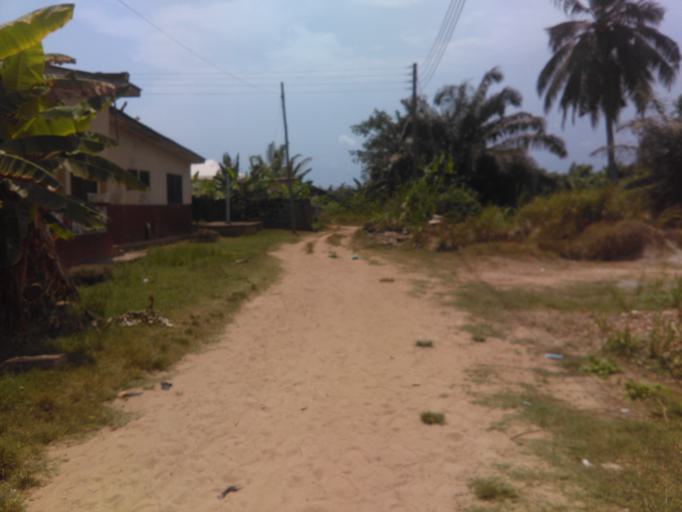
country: GH
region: Central
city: Cape Coast
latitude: 5.1046
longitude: -1.2909
